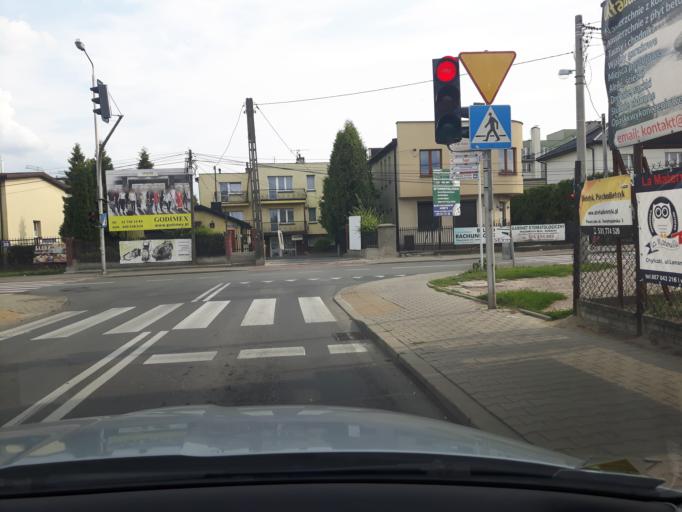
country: PL
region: Masovian Voivodeship
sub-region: Powiat piaseczynski
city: Piaseczno
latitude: 52.0748
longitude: 21.0168
